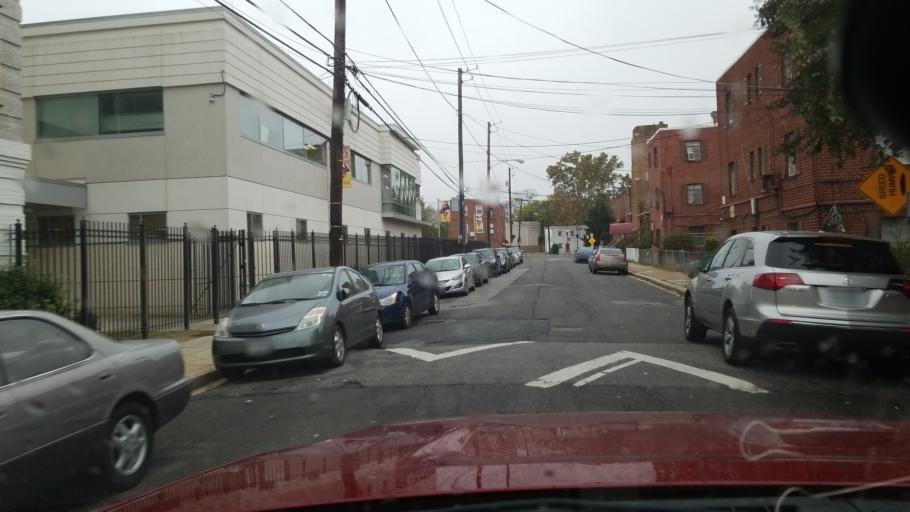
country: US
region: Maryland
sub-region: Prince George's County
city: Fairmount Heights
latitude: 38.9042
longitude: -76.9375
